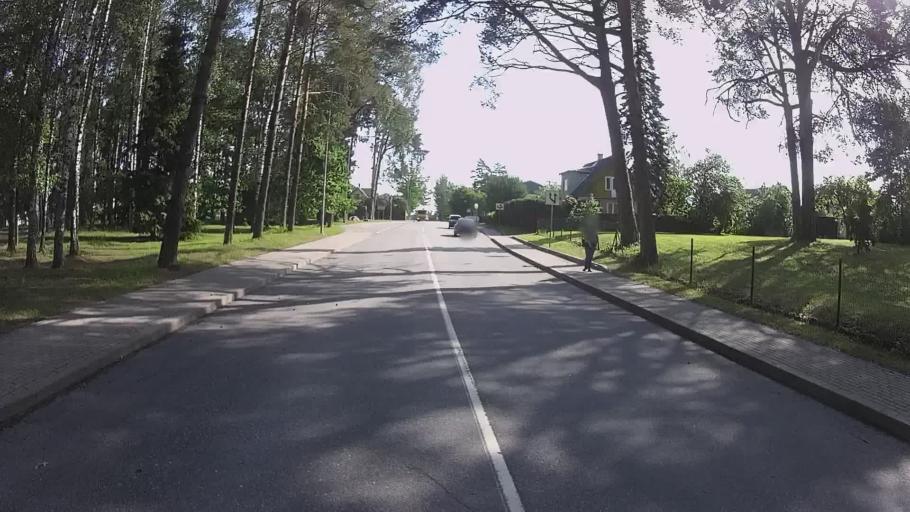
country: EE
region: Valgamaa
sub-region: Torva linn
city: Torva
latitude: 58.0056
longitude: 25.9290
